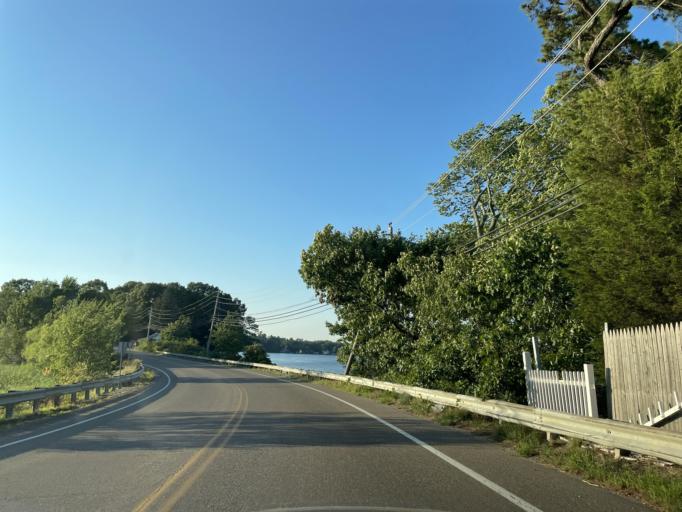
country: US
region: Massachusetts
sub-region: Plymouth County
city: Halifax
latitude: 42.0052
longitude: -70.8405
